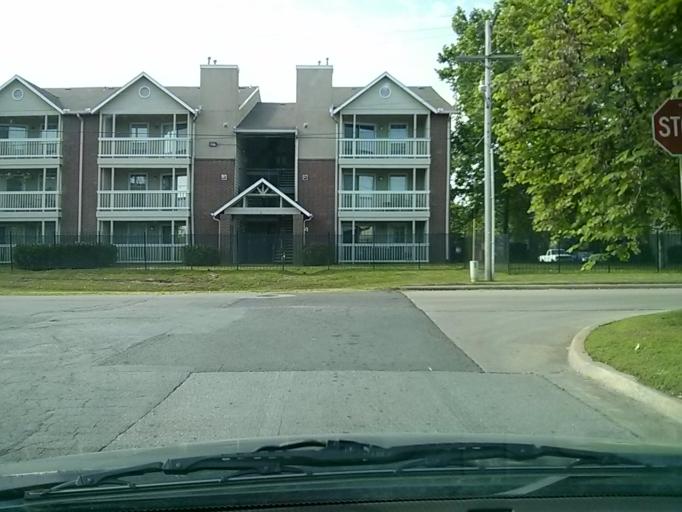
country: US
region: Oklahoma
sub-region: Tulsa County
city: Jenks
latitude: 36.0676
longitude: -95.9781
